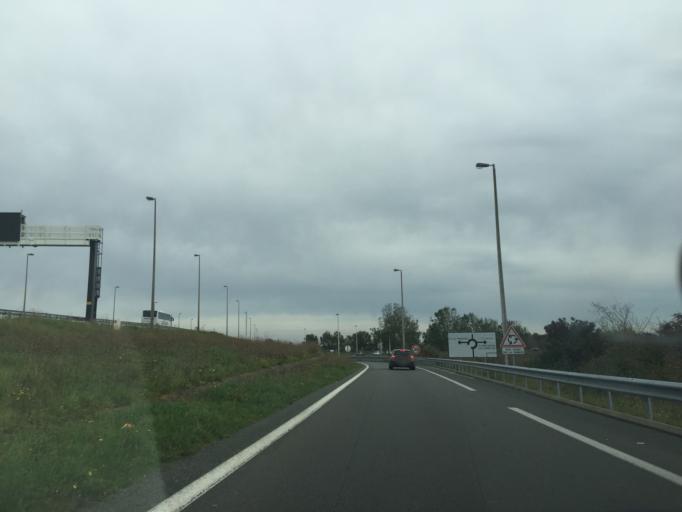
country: FR
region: Nord-Pas-de-Calais
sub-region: Departement du Pas-de-Calais
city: Frethun
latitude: 50.9395
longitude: 1.8342
